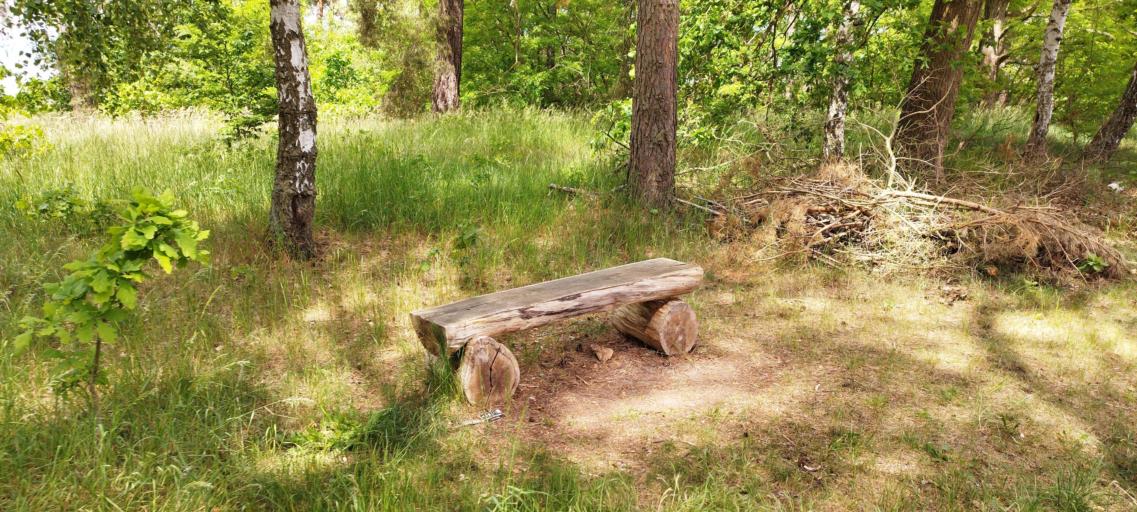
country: DE
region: Brandenburg
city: Wandlitz
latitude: 52.7200
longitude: 13.4258
